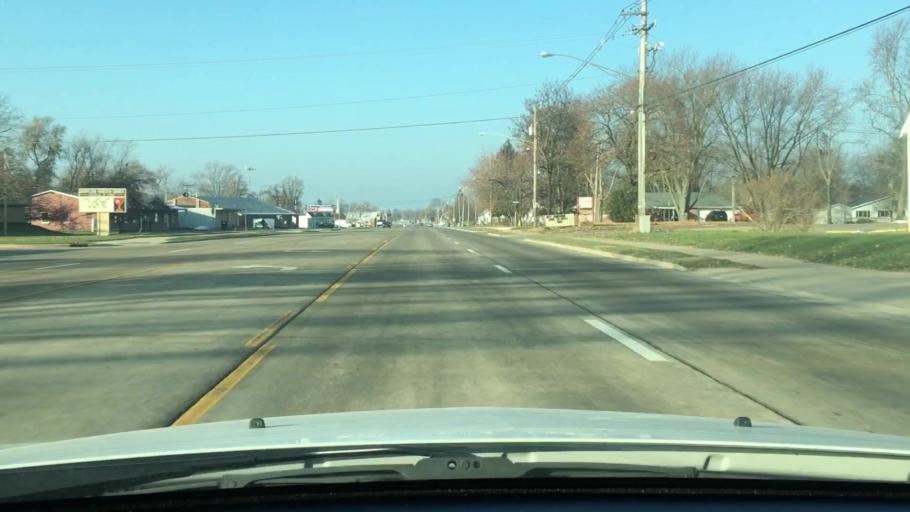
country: US
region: Illinois
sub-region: Woodford County
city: Germantown Hills
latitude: 40.6916
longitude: -89.4931
